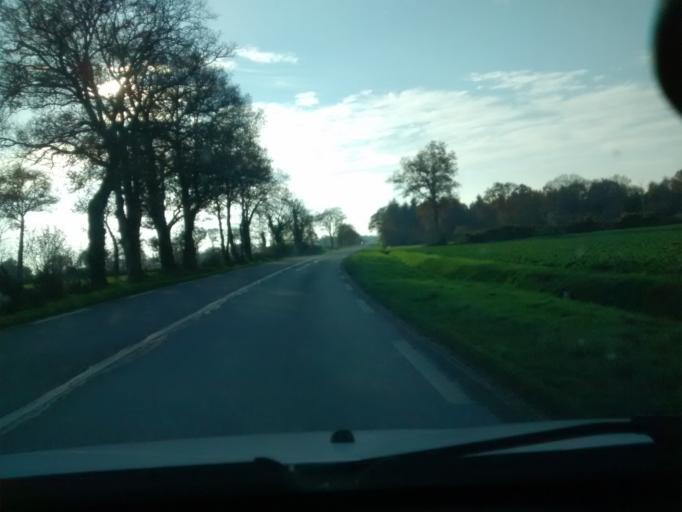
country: FR
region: Brittany
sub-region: Departement d'Ille-et-Vilaine
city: Sens-de-Bretagne
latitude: 48.3065
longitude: -1.5433
